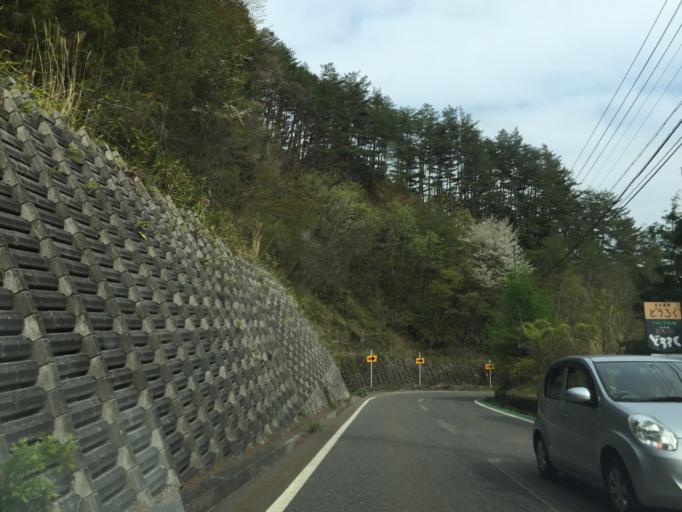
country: JP
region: Nagano
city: Iida
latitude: 35.2793
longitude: 137.6999
